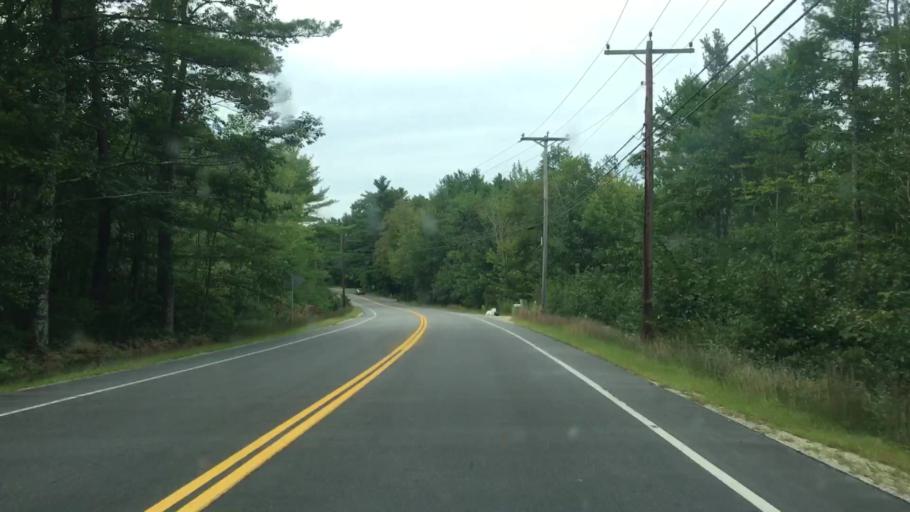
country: US
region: New Hampshire
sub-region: Strafford County
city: Madbury
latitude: 43.2045
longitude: -70.9693
